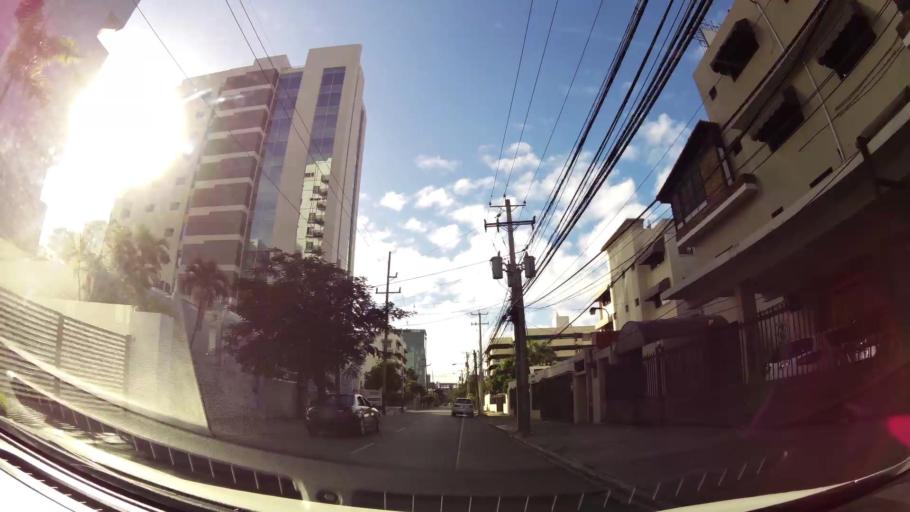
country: DO
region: Nacional
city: La Julia
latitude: 18.4689
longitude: -69.9371
